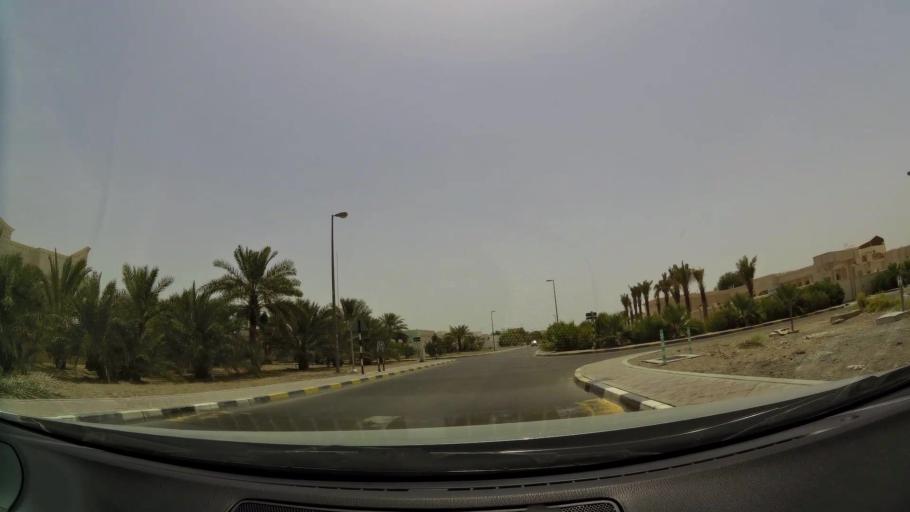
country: AE
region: Abu Dhabi
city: Al Ain
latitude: 24.1996
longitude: 55.7322
